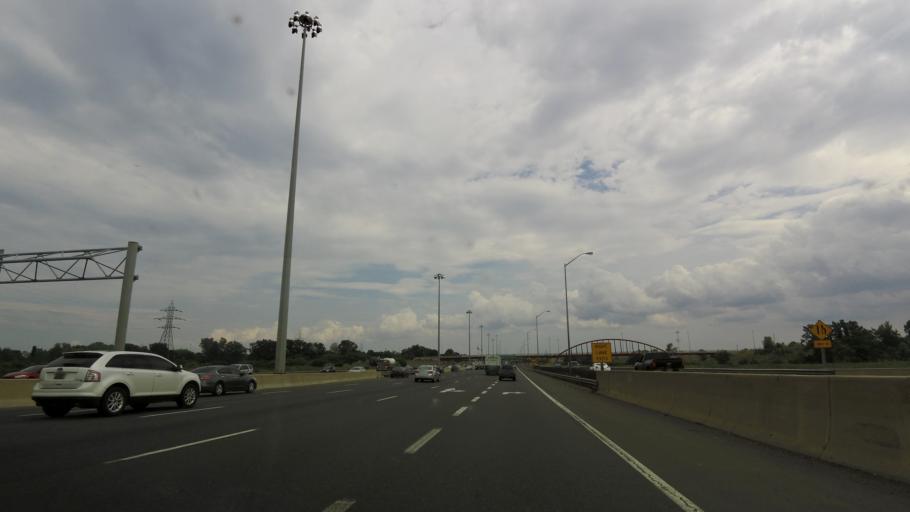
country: CA
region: Ontario
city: Hamilton
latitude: 43.2548
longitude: -79.7658
